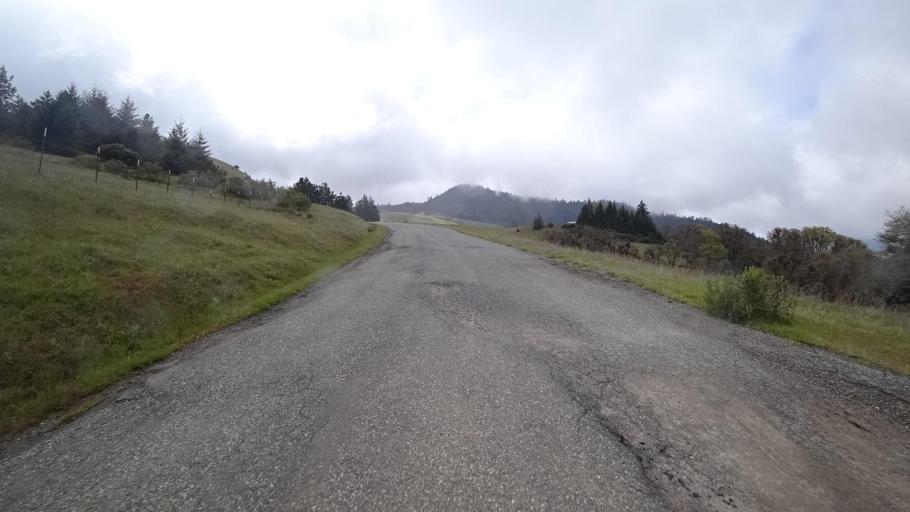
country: US
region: California
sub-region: Humboldt County
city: Redway
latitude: 40.1556
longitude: -123.5418
